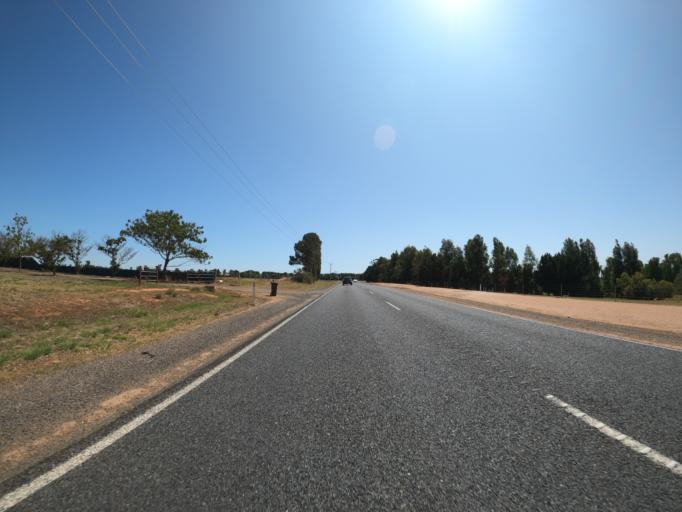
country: AU
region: Victoria
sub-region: Moira
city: Yarrawonga
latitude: -36.0275
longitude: 146.0776
